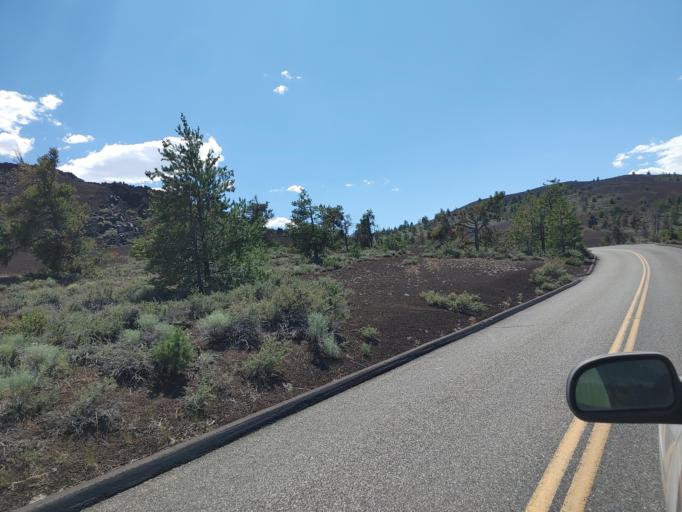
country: US
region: Idaho
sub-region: Butte County
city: Arco
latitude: 43.4536
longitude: -113.5532
